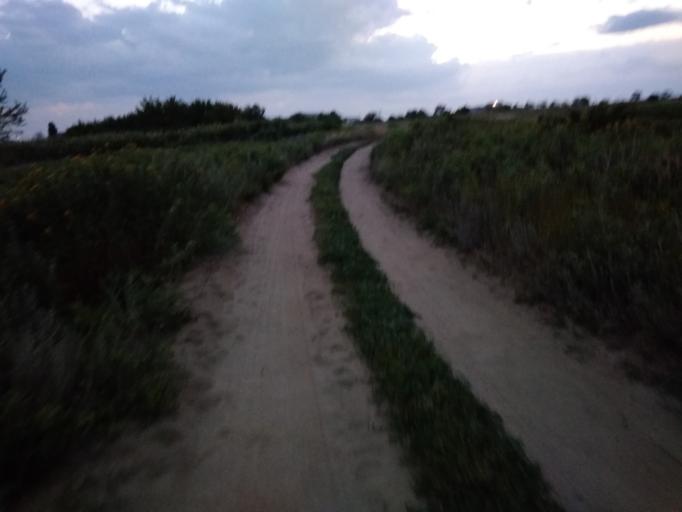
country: RU
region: Volgograd
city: Vodstroy
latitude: 48.8034
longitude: 44.5386
